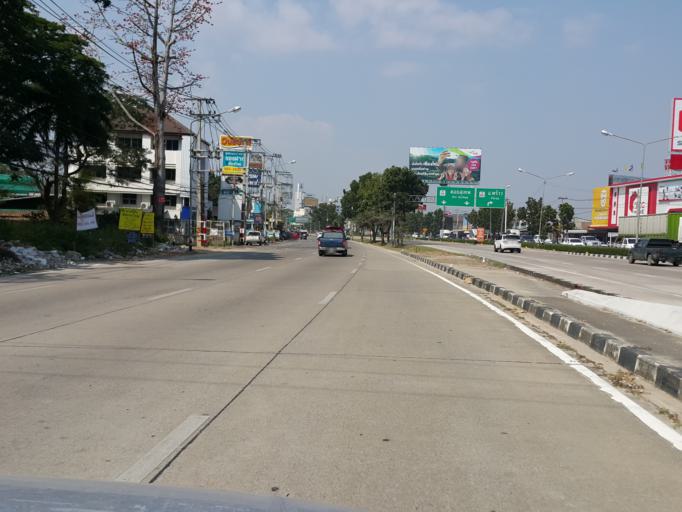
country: TH
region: Chiang Mai
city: Chiang Mai
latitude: 18.8069
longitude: 99.0160
